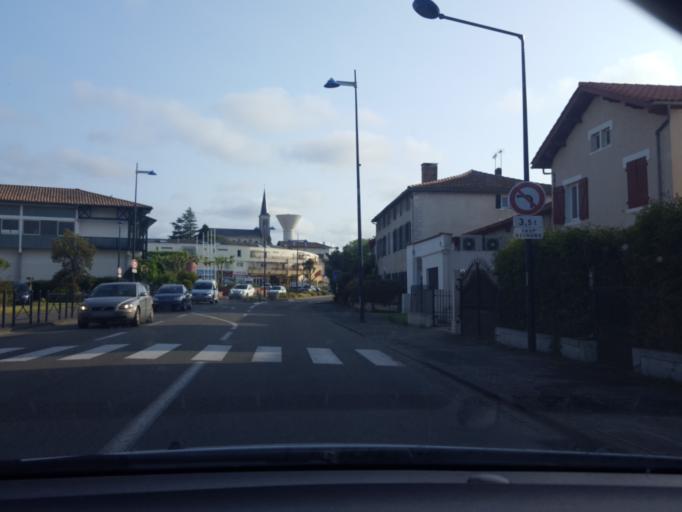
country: FR
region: Aquitaine
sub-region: Departement des Landes
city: Ondres
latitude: 43.5635
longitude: -1.4462
